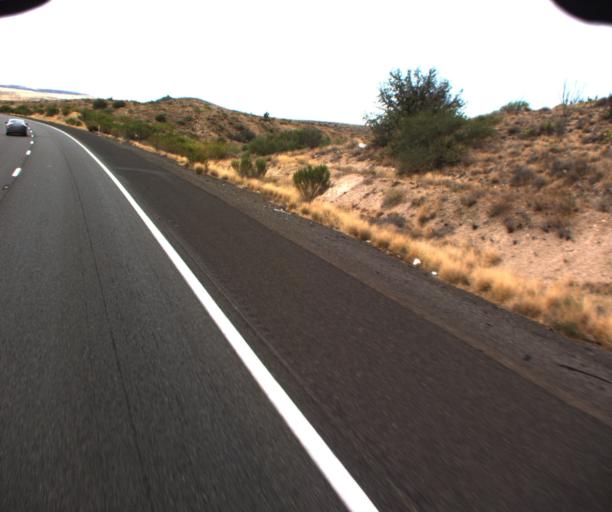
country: US
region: Arizona
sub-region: Yavapai County
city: Cordes Lakes
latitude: 34.2604
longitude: -112.1172
